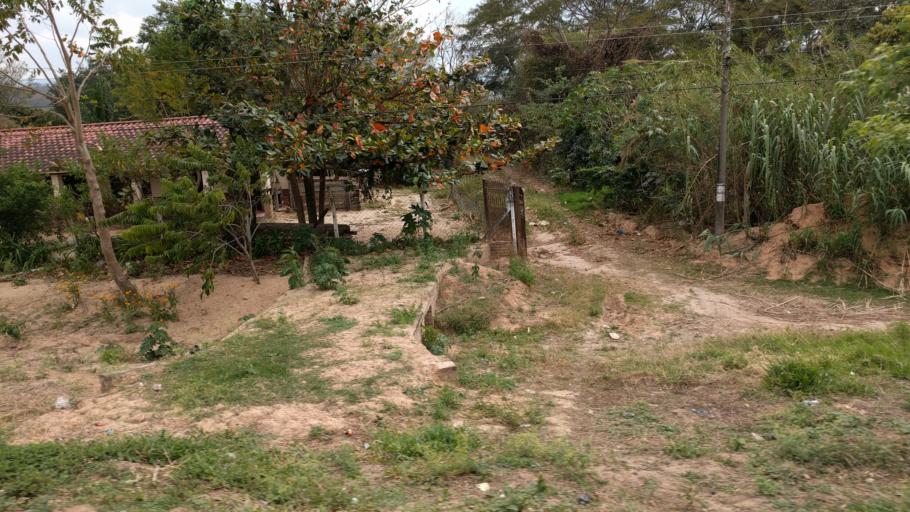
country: BO
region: Santa Cruz
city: Jorochito
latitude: -18.1149
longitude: -63.4603
